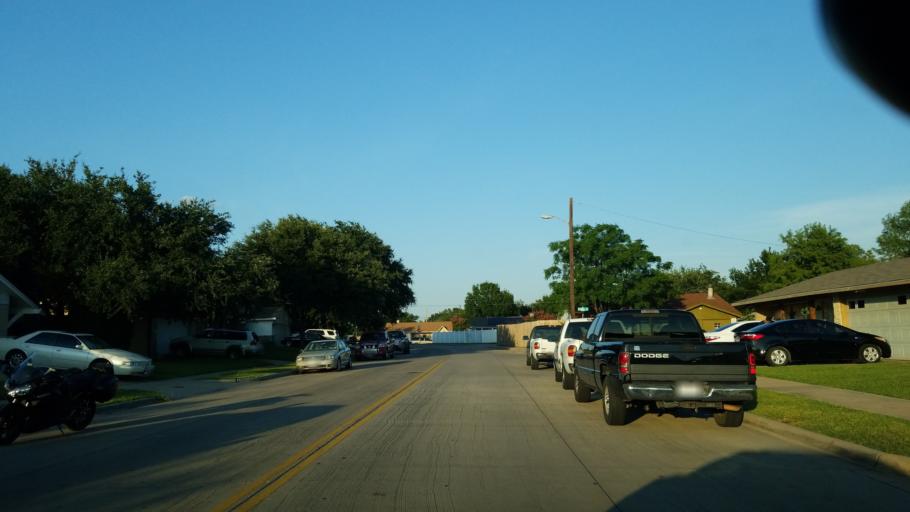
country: US
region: Texas
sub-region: Dallas County
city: Carrollton
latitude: 32.9493
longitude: -96.8885
